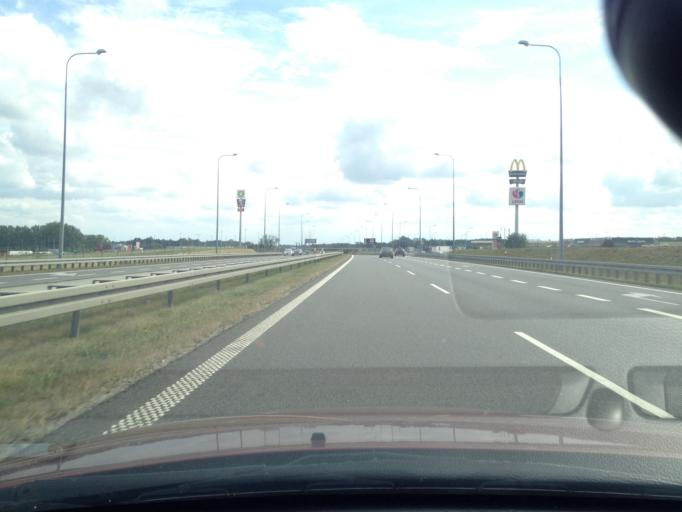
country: PL
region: West Pomeranian Voivodeship
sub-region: Powiat gryfinski
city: Gryfino
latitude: 53.3090
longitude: 14.5810
